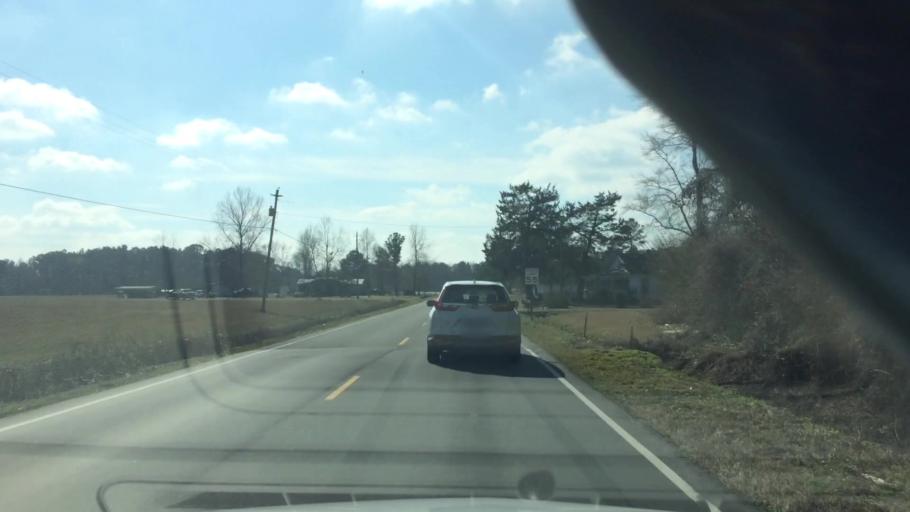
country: US
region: North Carolina
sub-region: Duplin County
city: Beulaville
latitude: 34.8843
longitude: -77.7869
